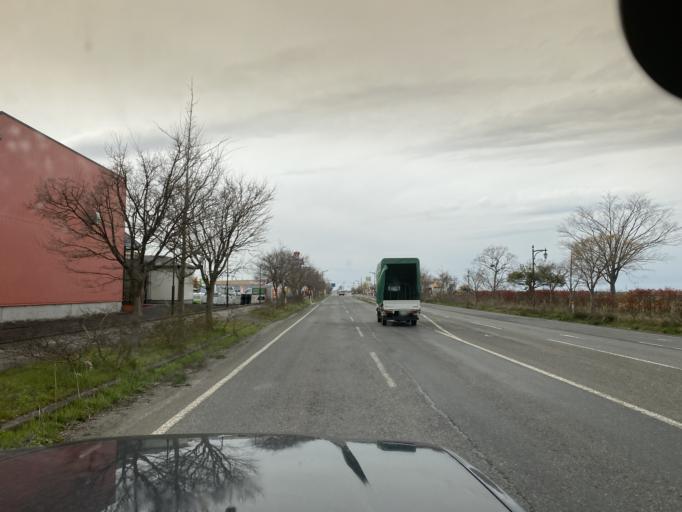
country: JP
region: Niigata
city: Niitsu-honcho
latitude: 37.8152
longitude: 139.1056
